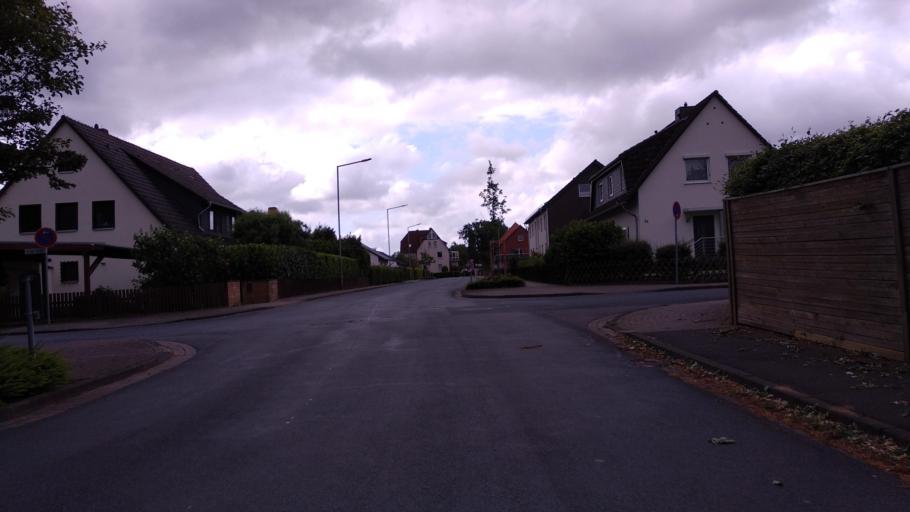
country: DE
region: Lower Saxony
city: Hagenburg
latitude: 52.4567
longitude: 9.3680
